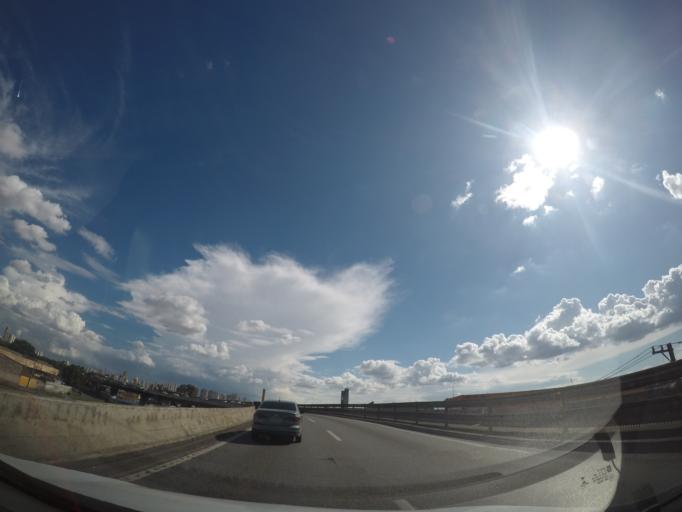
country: BR
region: Sao Paulo
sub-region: Sao Paulo
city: Sao Paulo
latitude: -23.5243
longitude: -46.5858
